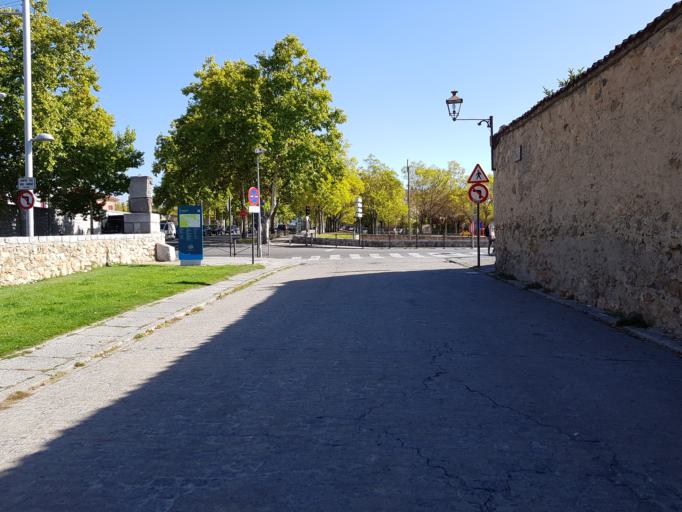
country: ES
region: Castille and Leon
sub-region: Provincia de Segovia
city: Segovia
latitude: 40.9446
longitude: -4.1106
